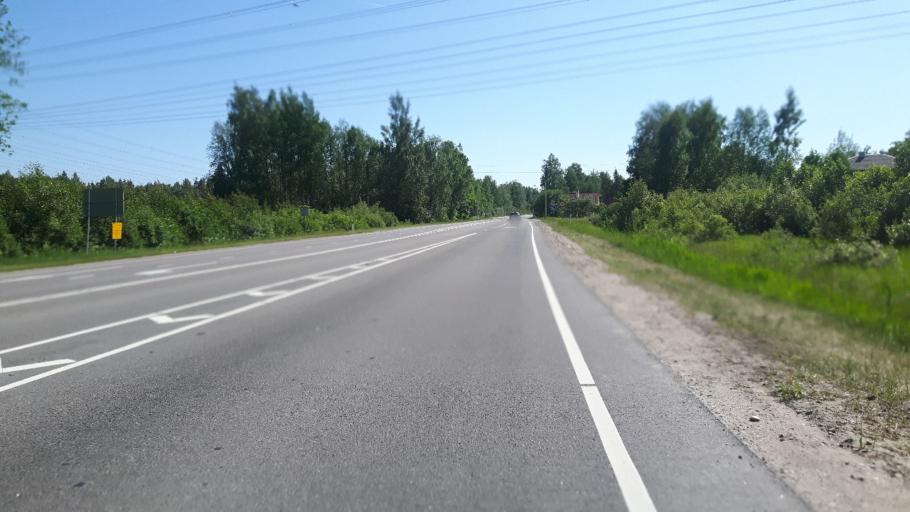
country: EE
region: Paernumaa
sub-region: Paikuse vald
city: Paikuse
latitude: 58.3900
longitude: 24.6413
